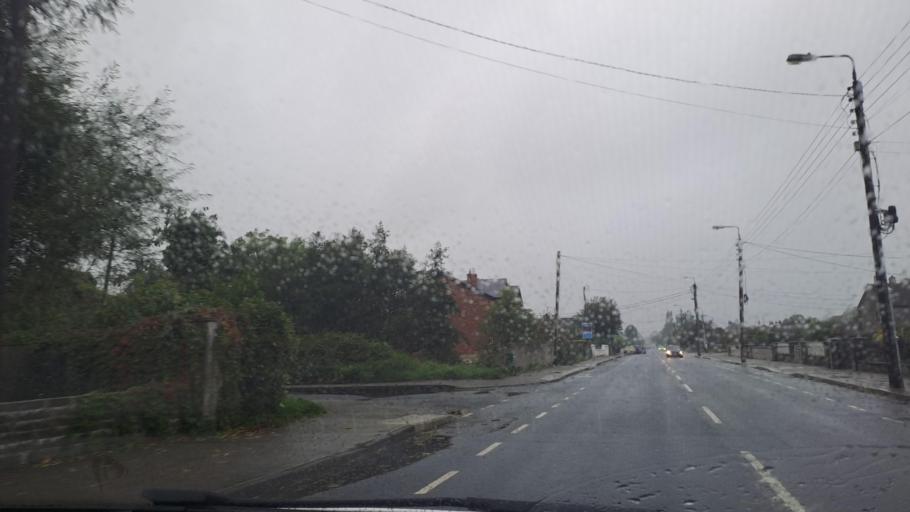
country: IE
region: Leinster
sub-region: Lu
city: Dundalk
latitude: 53.9947
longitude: -6.3880
